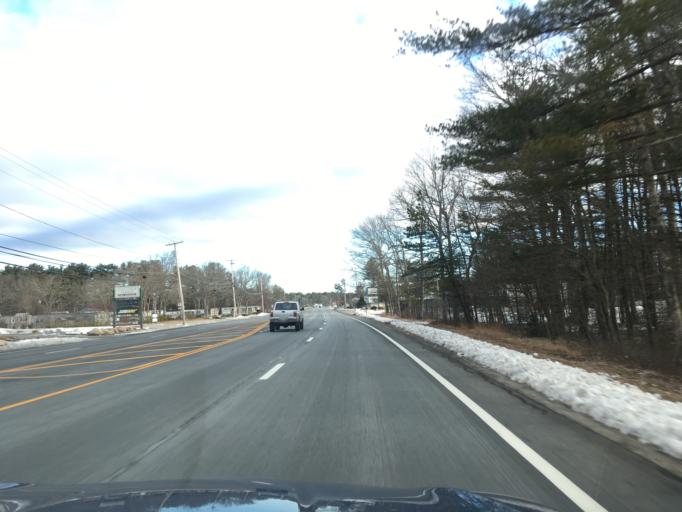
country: US
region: Rhode Island
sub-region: Kent County
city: West Greenwich
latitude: 41.6626
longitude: -71.6021
